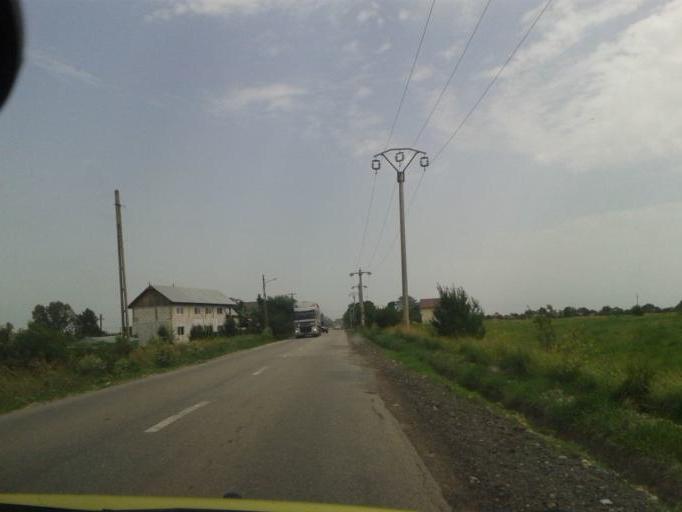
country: RO
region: Dambovita
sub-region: Comuna Petresti
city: Petresti
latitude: 44.6732
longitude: 25.3098
